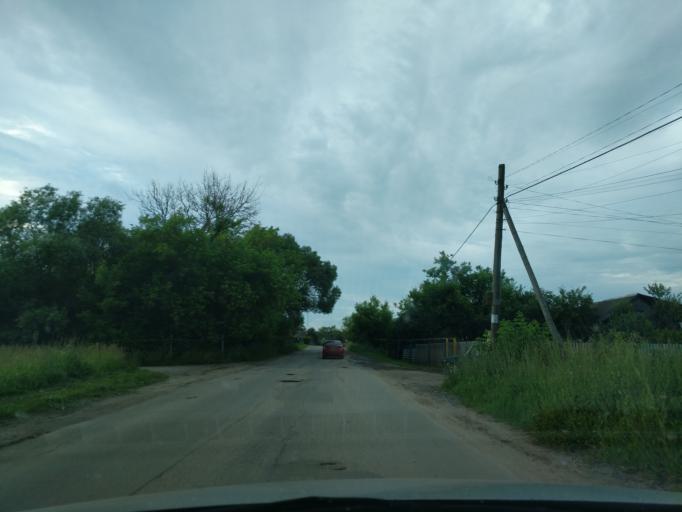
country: RU
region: Kaluga
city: Myatlevo
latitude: 54.7971
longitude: 35.7398
